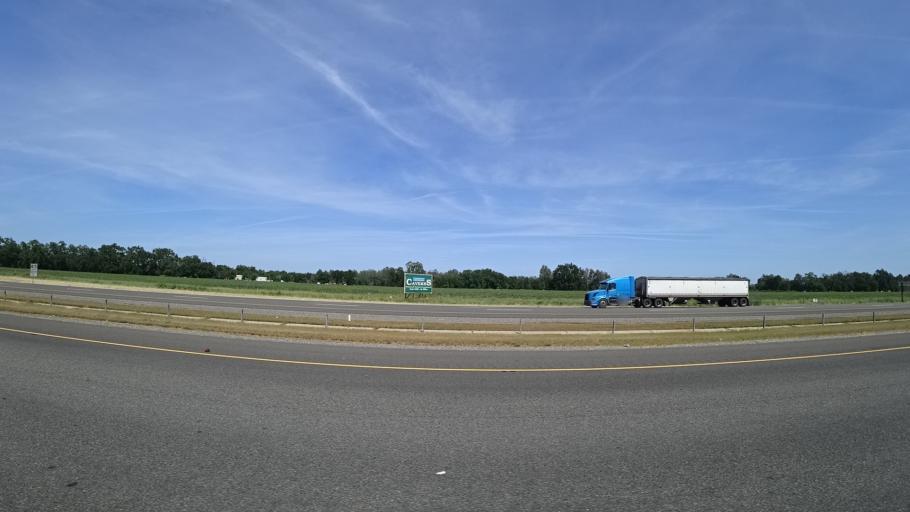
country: US
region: California
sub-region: Shasta County
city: Redding
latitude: 40.5287
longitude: -122.3482
